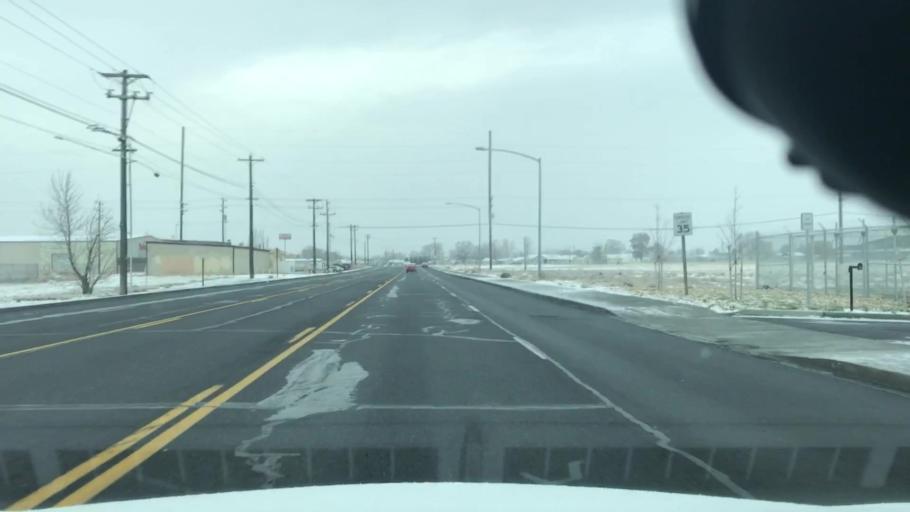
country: US
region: Washington
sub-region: Grant County
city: Moses Lake North
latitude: 47.1816
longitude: -119.3227
